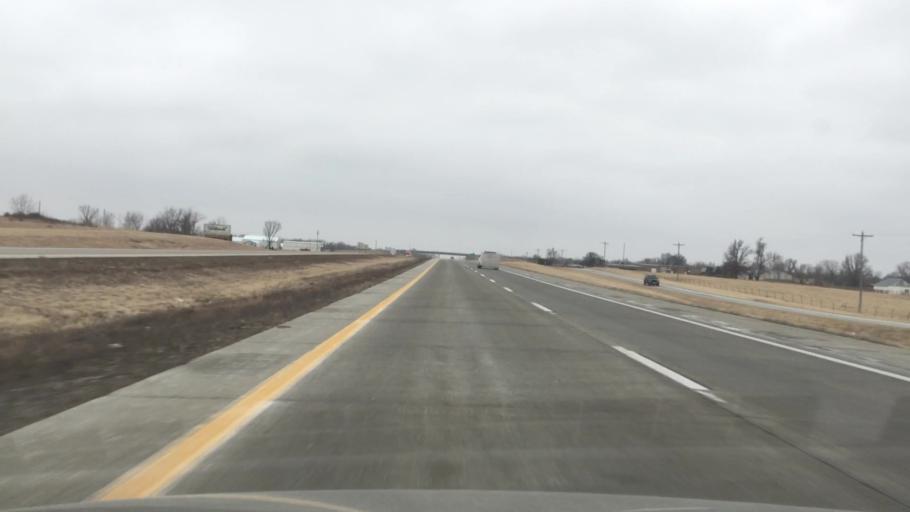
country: US
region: Missouri
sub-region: Cass County
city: Harrisonville
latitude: 38.6110
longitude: -94.3488
